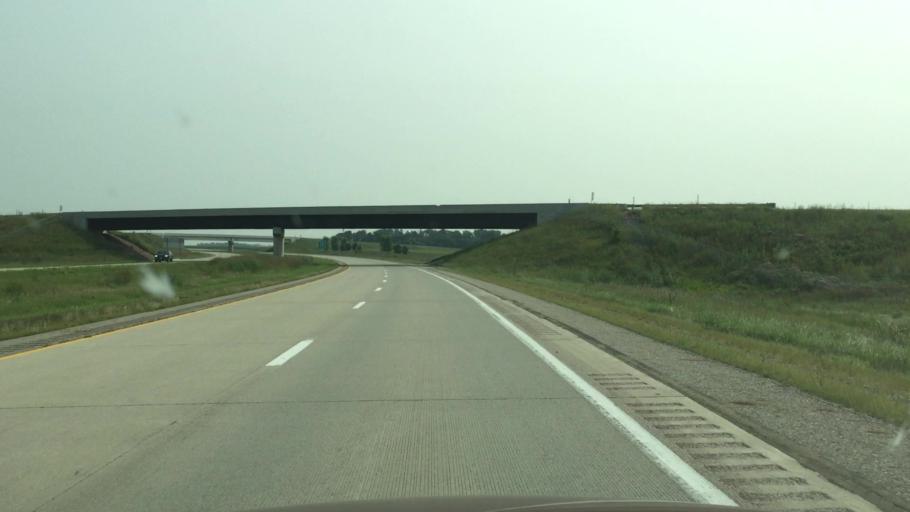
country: US
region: Iowa
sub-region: Osceola County
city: Sibley
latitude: 43.3865
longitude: -95.7232
